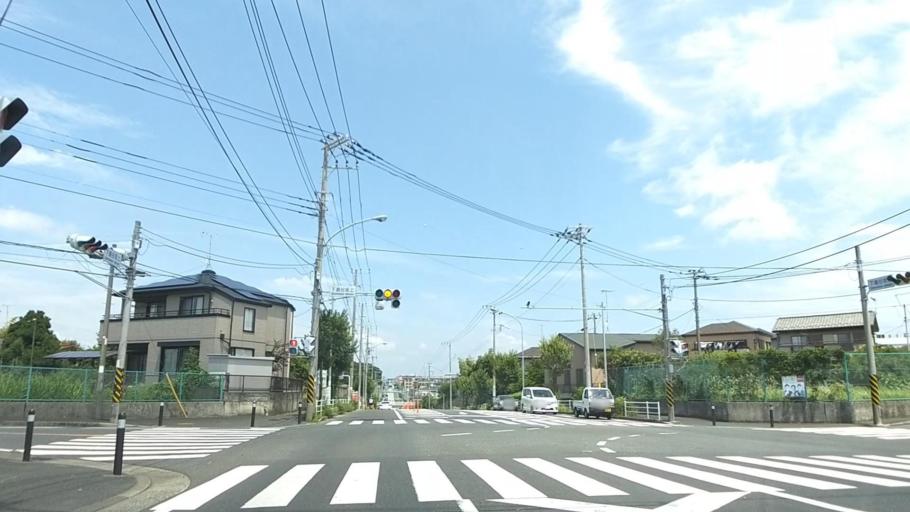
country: JP
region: Kanagawa
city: Minami-rinkan
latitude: 35.4501
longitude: 139.4836
